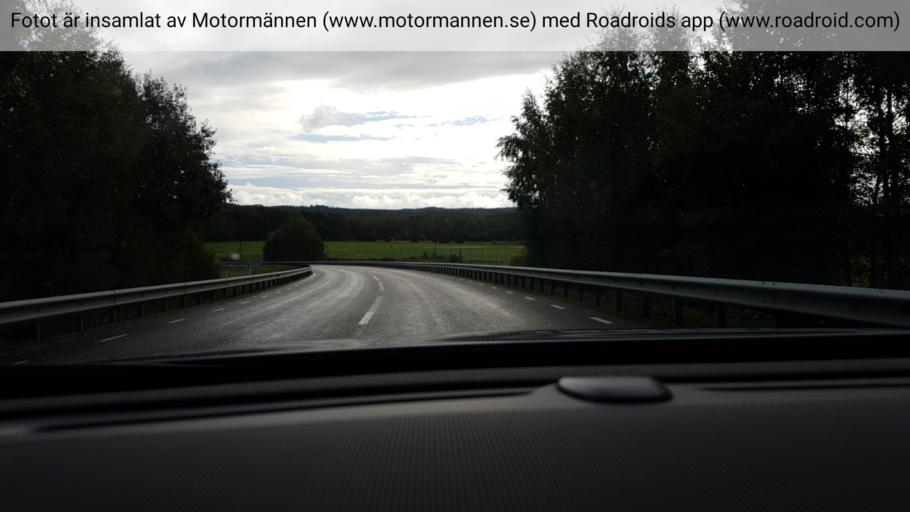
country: SE
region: Vaestra Goetaland
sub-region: Marks Kommun
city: Kinna
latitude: 57.4785
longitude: 12.6915
